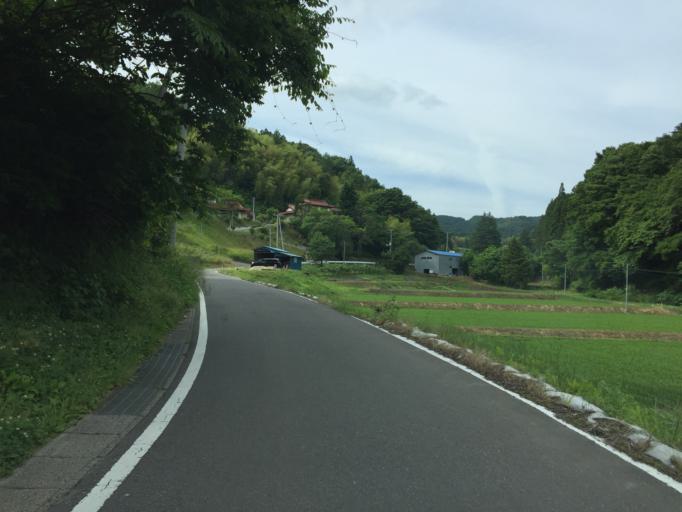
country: JP
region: Fukushima
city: Funehikimachi-funehiki
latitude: 37.4513
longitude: 140.6405
